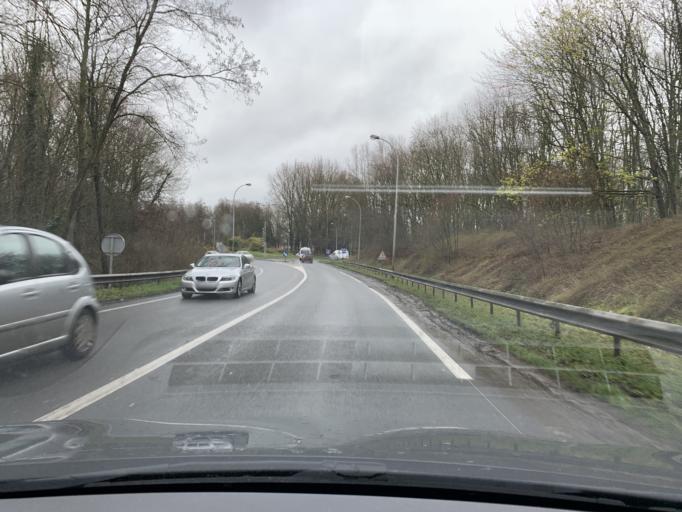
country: FR
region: Nord-Pas-de-Calais
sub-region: Departement du Nord
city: Sin-le-Noble
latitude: 50.3612
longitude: 3.1240
